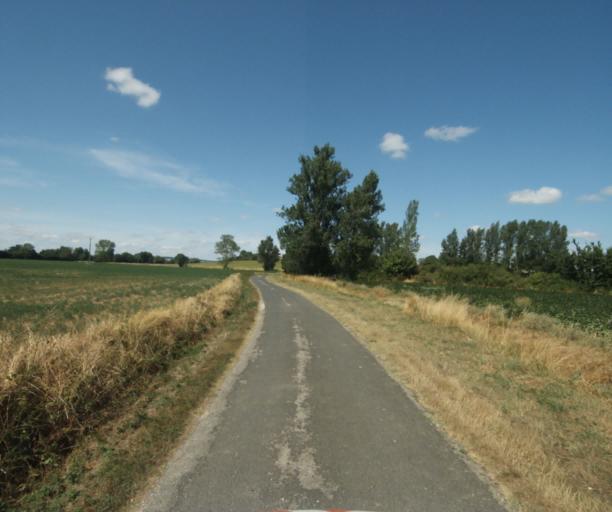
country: FR
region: Midi-Pyrenees
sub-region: Departement de la Haute-Garonne
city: Revel
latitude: 43.4944
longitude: 1.9935
